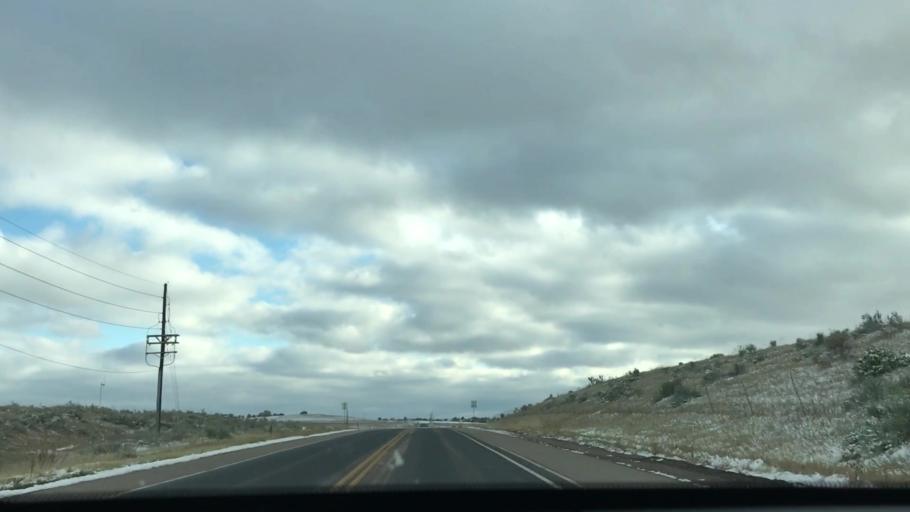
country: US
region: Colorado
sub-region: Boulder County
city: Lafayette
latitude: 39.9696
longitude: -105.0719
